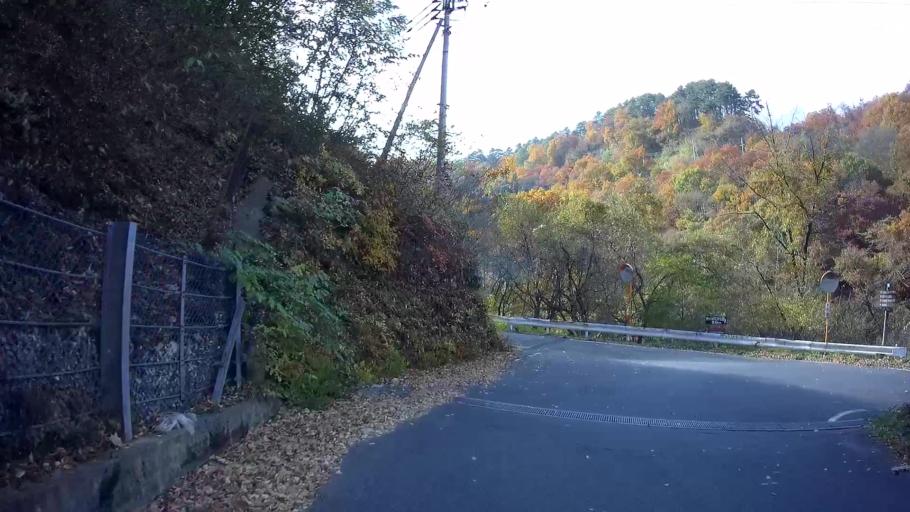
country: JP
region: Gunma
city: Nakanojomachi
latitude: 36.6271
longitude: 138.6321
